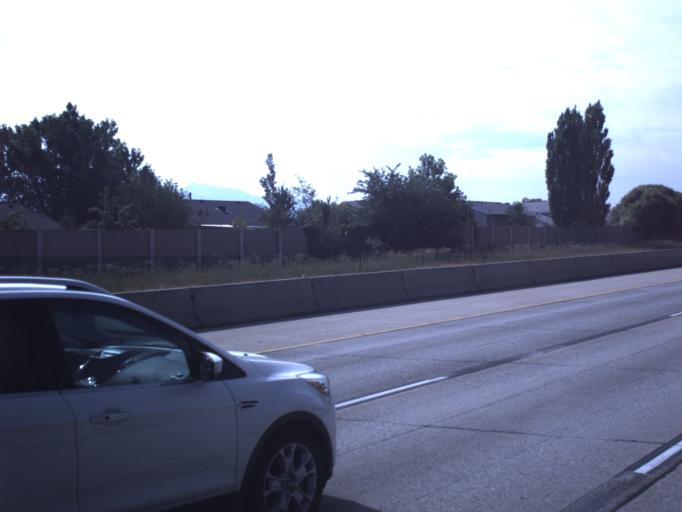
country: US
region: Utah
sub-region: Salt Lake County
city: West Valley City
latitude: 40.6914
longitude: -111.9818
